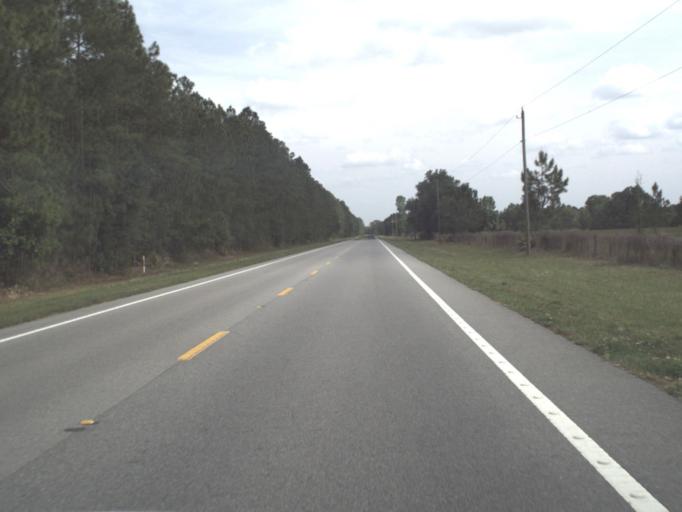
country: US
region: Florida
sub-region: Putnam County
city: Crescent City
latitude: 29.5254
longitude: -81.5103
